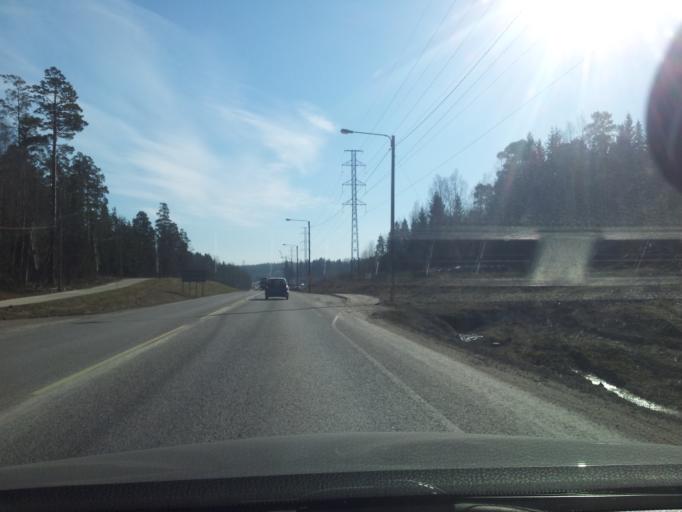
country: FI
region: Uusimaa
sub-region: Helsinki
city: Espoo
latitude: 60.1791
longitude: 24.6102
